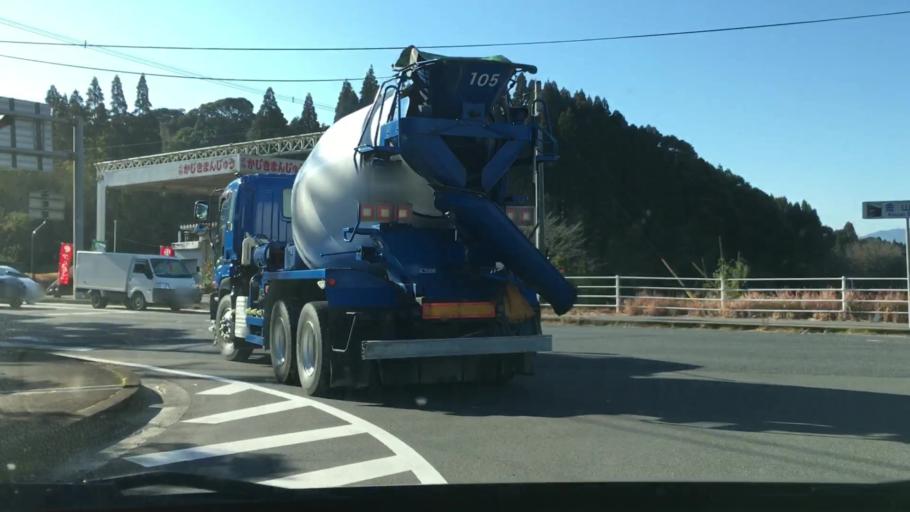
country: JP
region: Kagoshima
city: Kajiki
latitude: 31.7561
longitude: 130.6775
